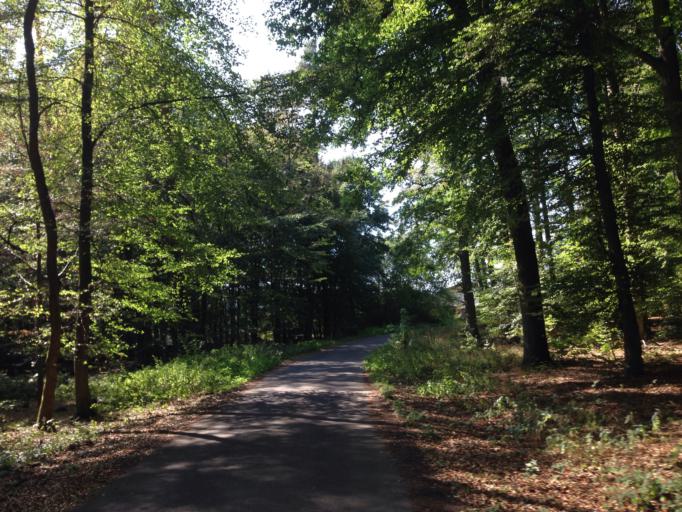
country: DE
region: Hesse
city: Staufenberg
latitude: 50.6459
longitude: 8.7447
